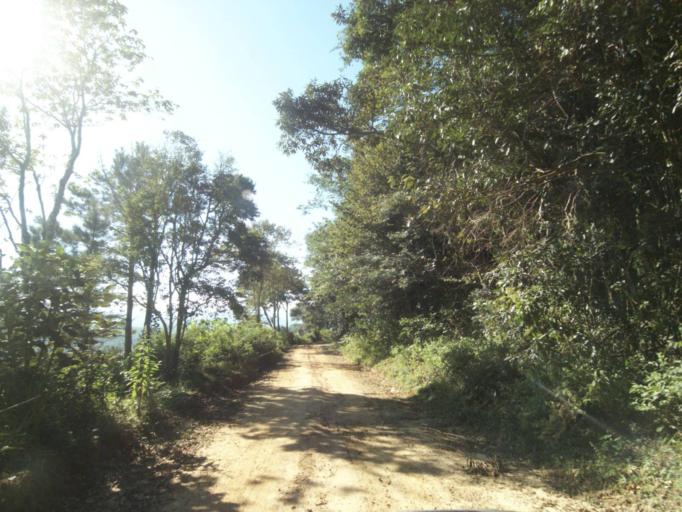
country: BR
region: Parana
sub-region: Tibagi
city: Tibagi
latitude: -24.5479
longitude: -50.4694
